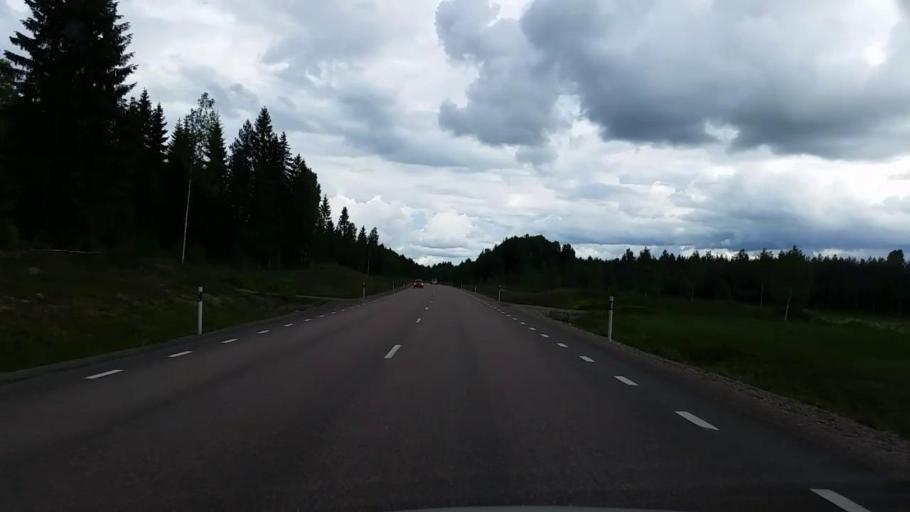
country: SE
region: Gaevleborg
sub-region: Hofors Kommun
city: Hofors
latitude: 60.4757
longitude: 16.4471
